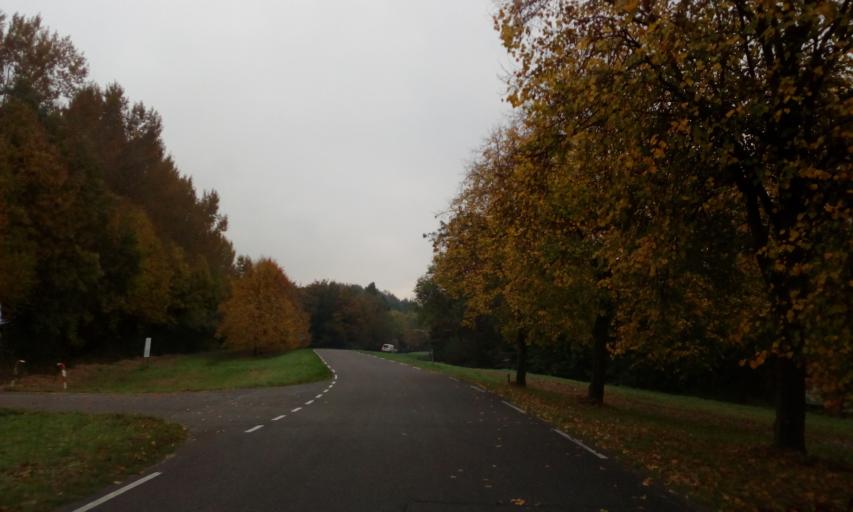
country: NL
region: South Holland
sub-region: Gemeente Lansingerland
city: Bleiswijk
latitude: 51.9778
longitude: 4.5557
